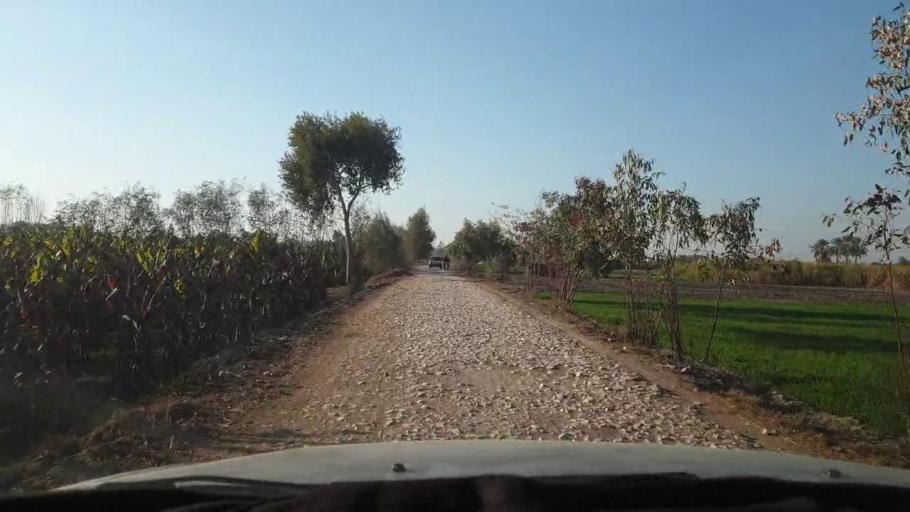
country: PK
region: Sindh
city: Adilpur
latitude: 27.9509
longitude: 69.2343
